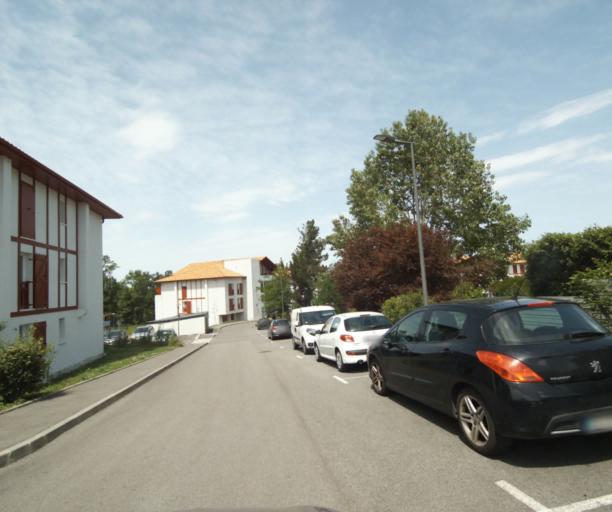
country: FR
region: Aquitaine
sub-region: Departement des Pyrenees-Atlantiques
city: Mouguerre
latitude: 43.4616
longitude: -1.4429
